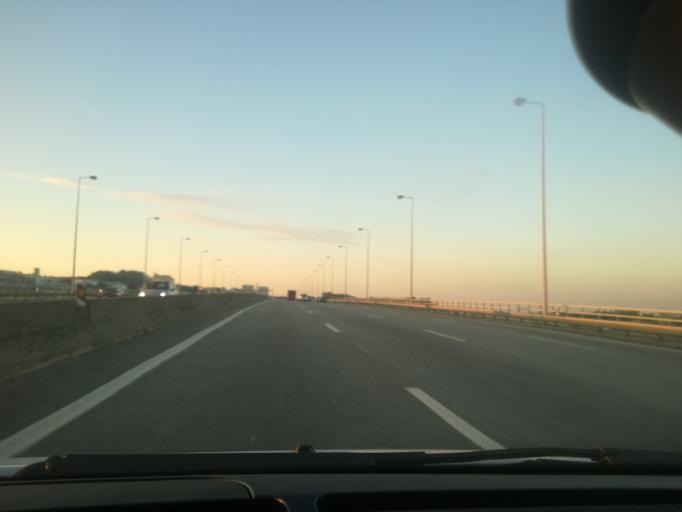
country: PT
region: Porto
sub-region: Vila Nova de Gaia
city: Oliveira do Douro
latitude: 41.1398
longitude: -8.5807
